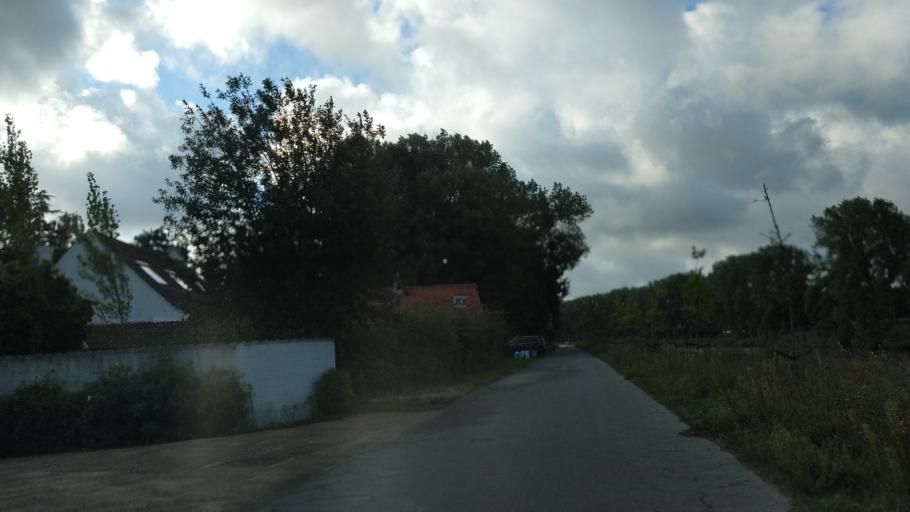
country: BE
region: Flanders
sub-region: Provincie Oost-Vlaanderen
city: Zomergem
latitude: 51.0842
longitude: 3.5634
